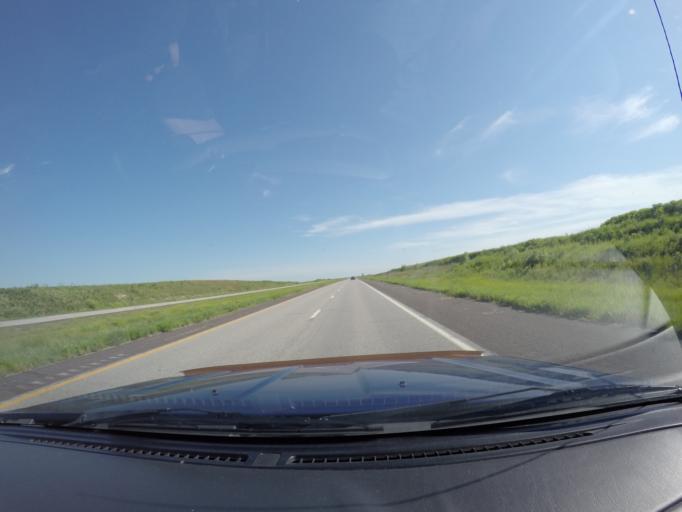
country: US
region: Kansas
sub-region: Riley County
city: Manhattan
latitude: 39.1076
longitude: -96.5384
